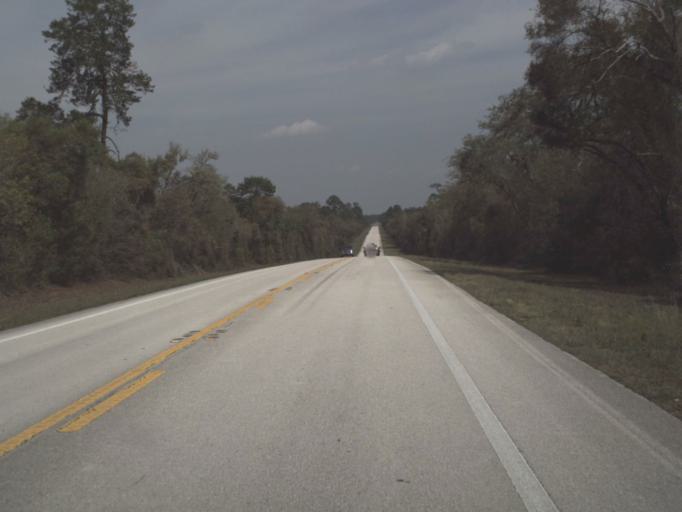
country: US
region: Florida
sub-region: Lake County
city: Astor
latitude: 29.1882
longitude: -81.6549
